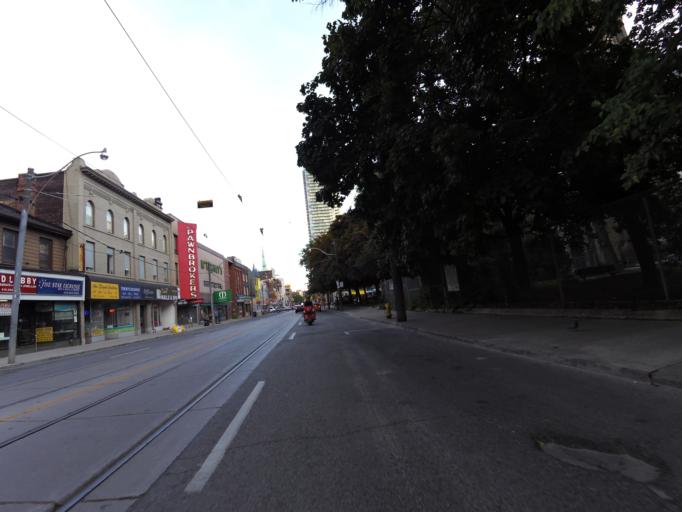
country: CA
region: Ontario
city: Toronto
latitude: 43.6542
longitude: -79.3762
